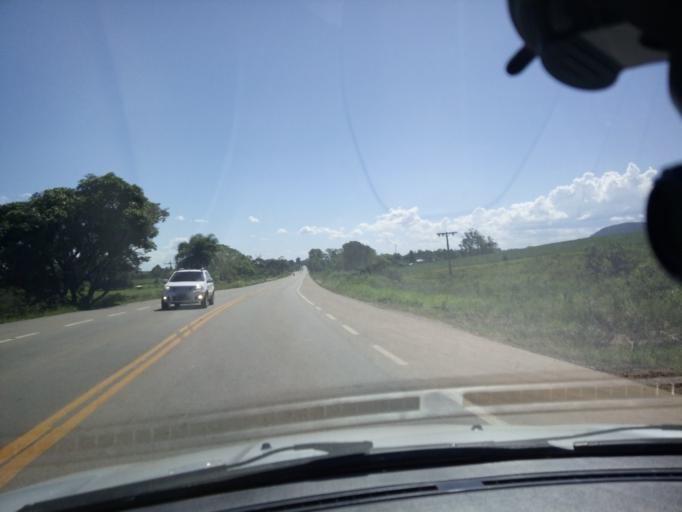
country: BR
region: Rio Grande do Sul
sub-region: Santa Maria
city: Santa Maria
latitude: -29.7331
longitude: -53.5243
